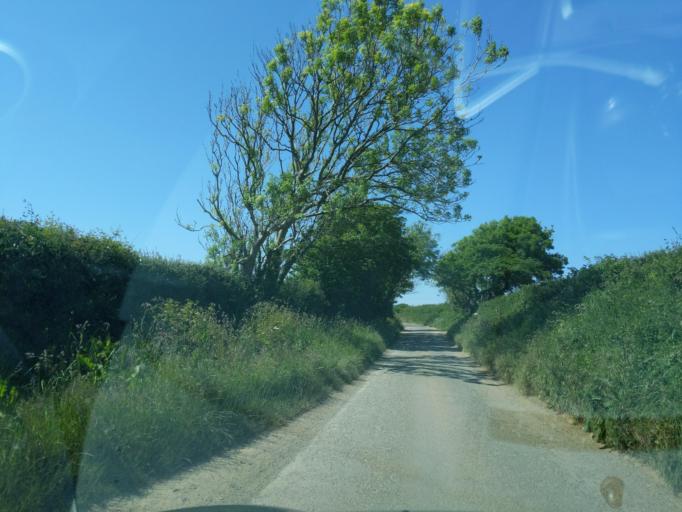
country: GB
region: England
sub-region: Cornwall
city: Wadebridge
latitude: 50.5787
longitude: -4.8319
